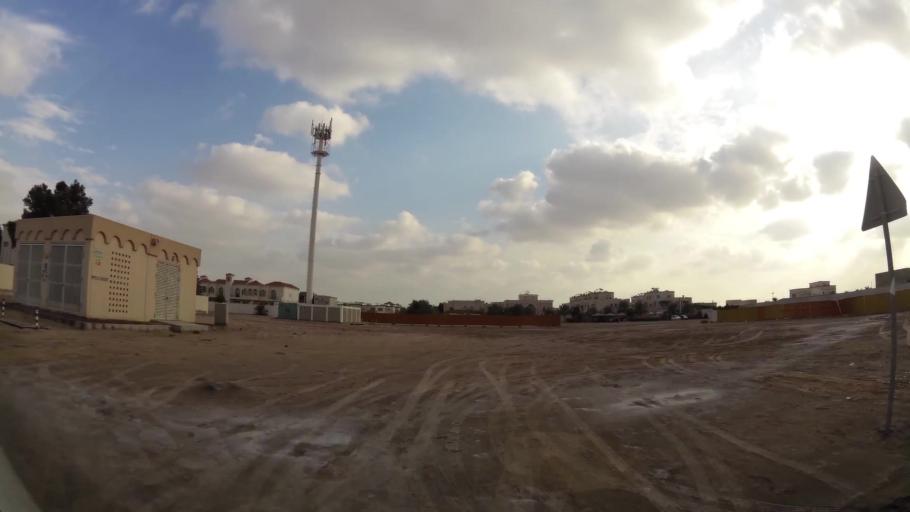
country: AE
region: Abu Dhabi
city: Abu Dhabi
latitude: 24.3708
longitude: 54.5421
